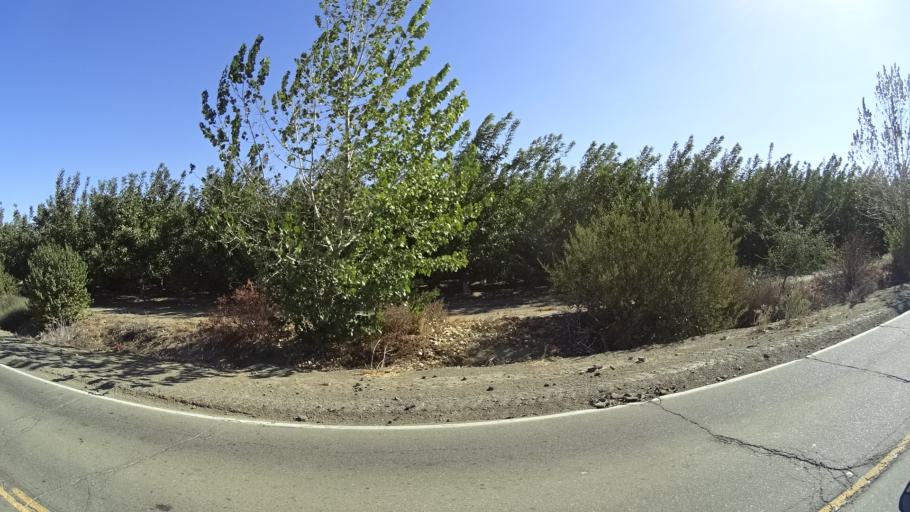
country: US
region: California
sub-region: Yolo County
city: Winters
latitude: 38.5765
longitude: -121.9714
